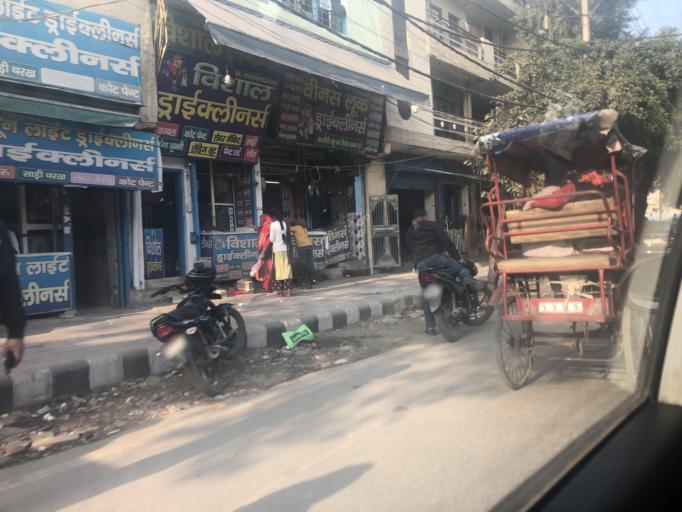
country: IN
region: Haryana
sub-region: Jhajjar
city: Bahadurgarh
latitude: 28.6136
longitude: 76.9801
